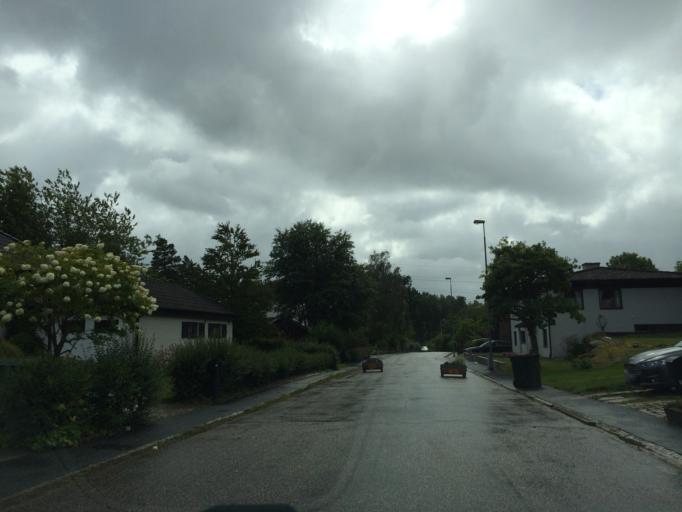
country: SE
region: Vaestra Goetaland
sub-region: Trollhattan
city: Trollhattan
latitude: 58.2800
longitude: 12.2702
